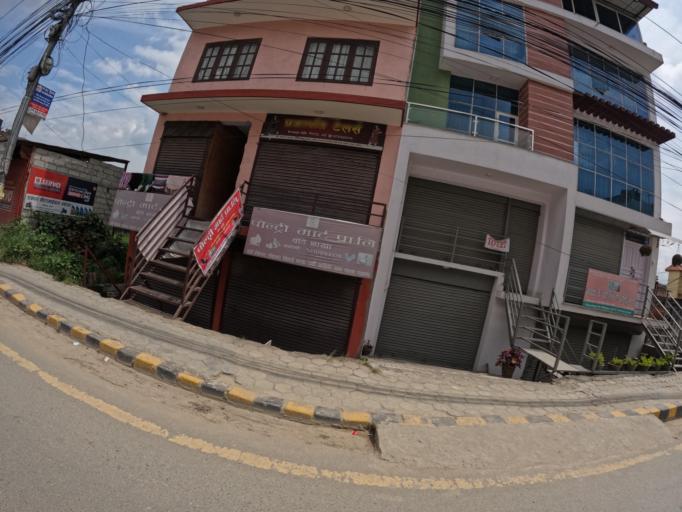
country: NP
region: Central Region
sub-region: Bagmati Zone
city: Bhaktapur
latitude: 27.6863
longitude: 85.3880
